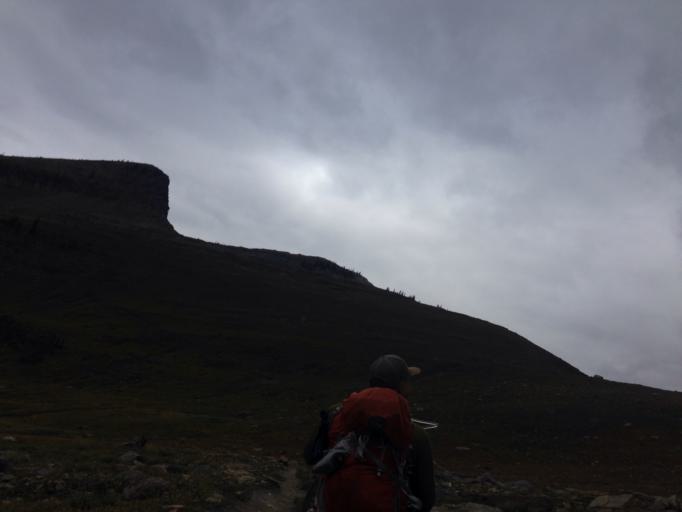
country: US
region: Montana
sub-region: Flathead County
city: Columbia Falls
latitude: 48.7336
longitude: -113.7213
